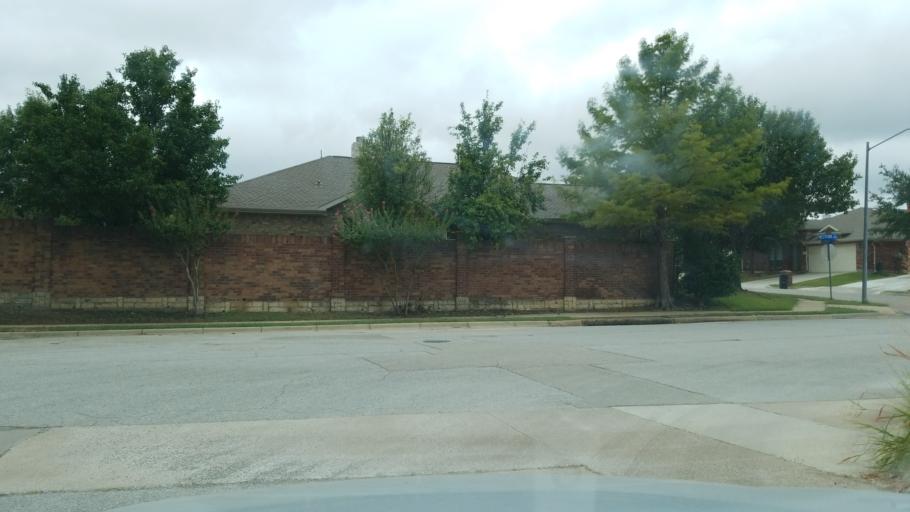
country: US
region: Texas
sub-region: Tarrant County
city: Bedford
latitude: 32.8347
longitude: -97.1142
